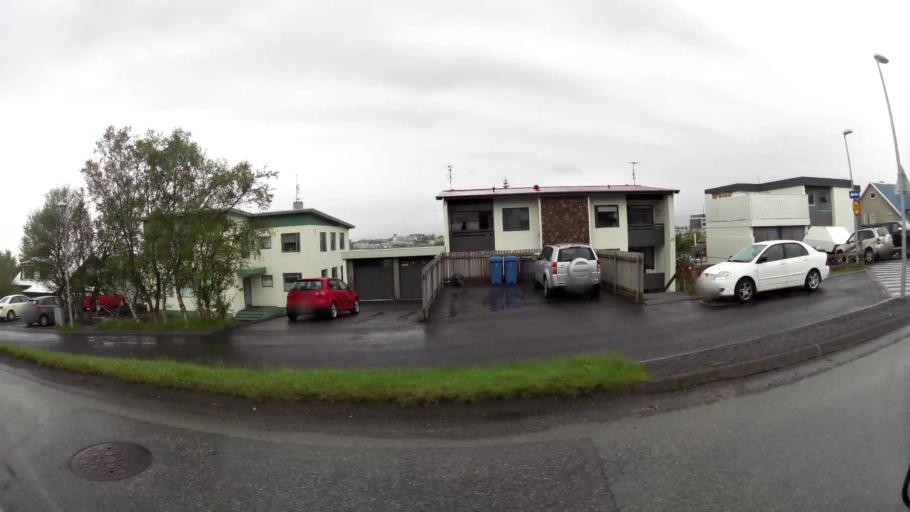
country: IS
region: Capital Region
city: Kopavogur
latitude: 64.1121
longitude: -21.8932
